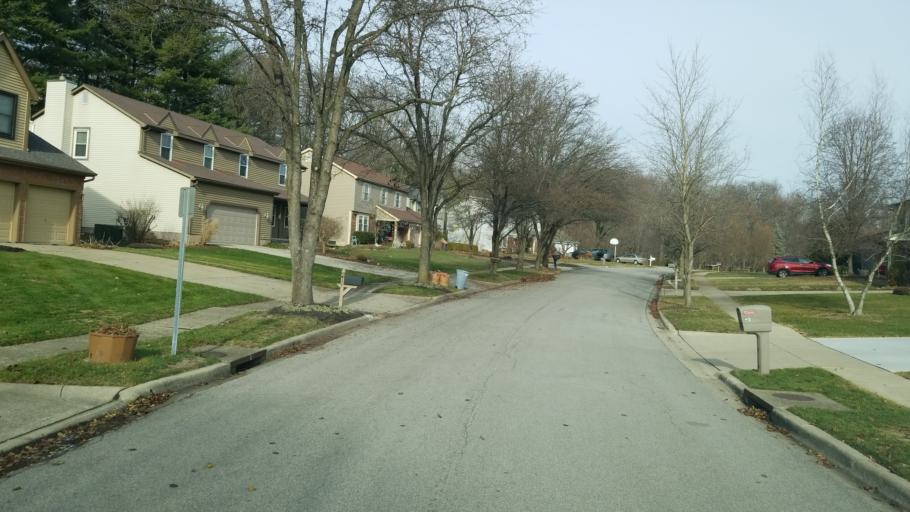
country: US
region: Ohio
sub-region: Delaware County
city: Powell
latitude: 40.1614
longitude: -83.0345
